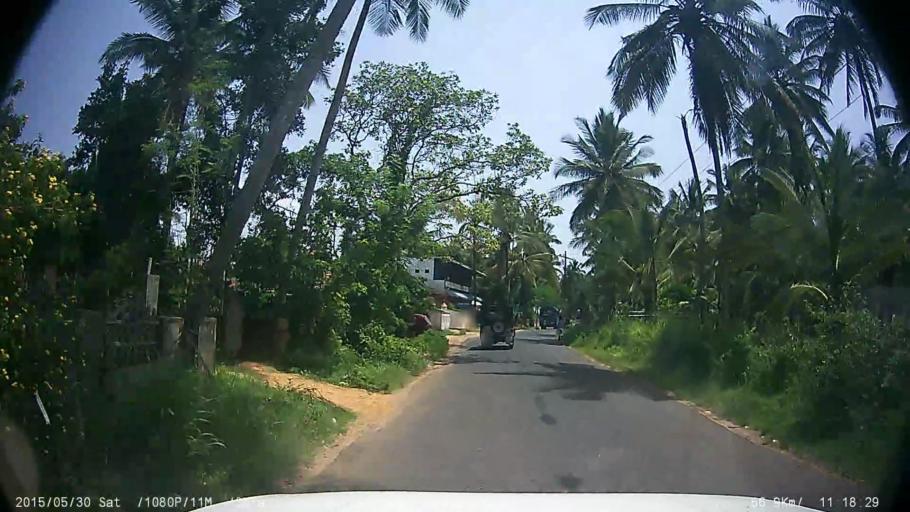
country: IN
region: Kerala
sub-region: Wayanad
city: Panamaram
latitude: 11.7849
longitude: 76.0453
